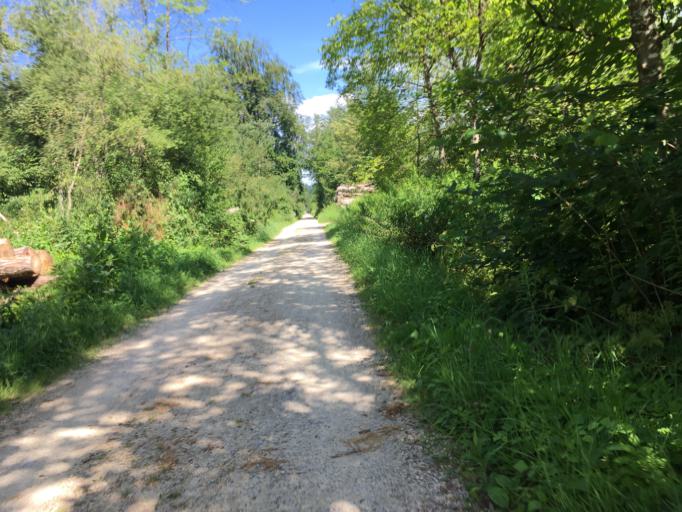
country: CH
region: Fribourg
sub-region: See District
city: Murten
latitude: 46.9474
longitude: 7.1346
